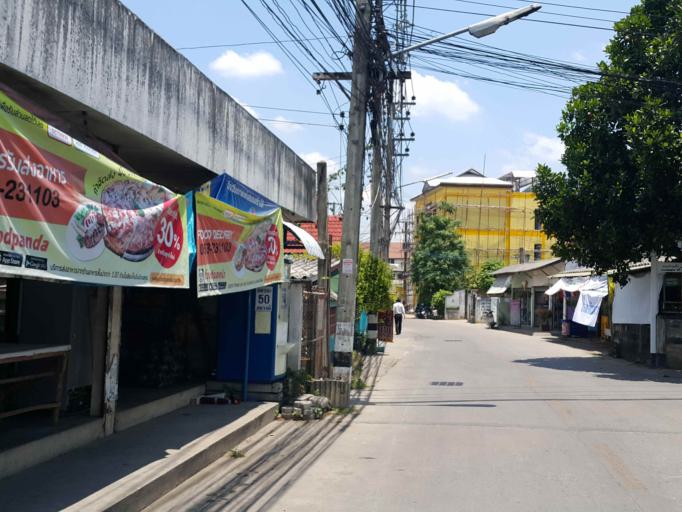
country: TH
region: Chiang Mai
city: Chiang Mai
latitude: 18.7656
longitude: 99.0106
